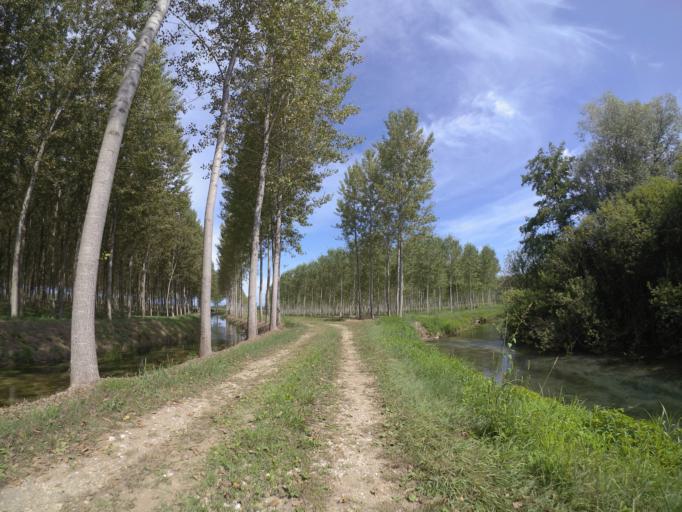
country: IT
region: Friuli Venezia Giulia
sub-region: Provincia di Udine
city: Varmo
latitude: 45.9145
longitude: 13.0203
